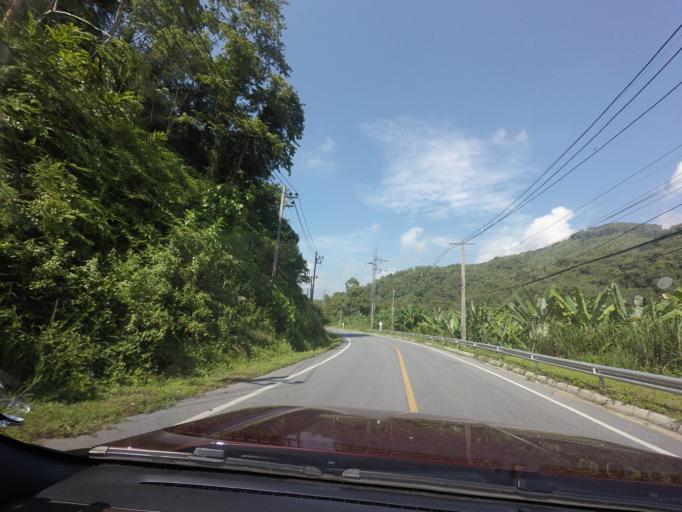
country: TH
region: Yala
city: Betong
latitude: 5.8968
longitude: 101.1465
